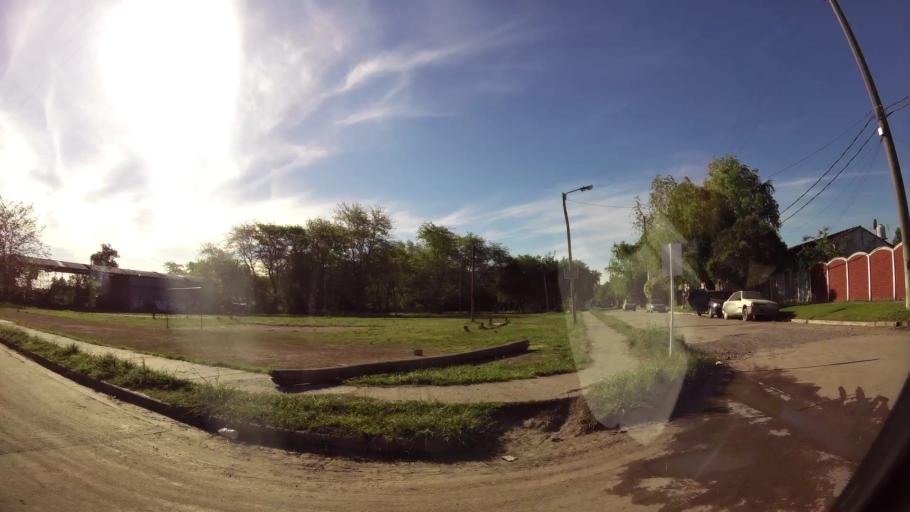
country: AR
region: Buenos Aires
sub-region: Partido de Almirante Brown
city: Adrogue
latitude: -34.8289
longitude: -58.3524
